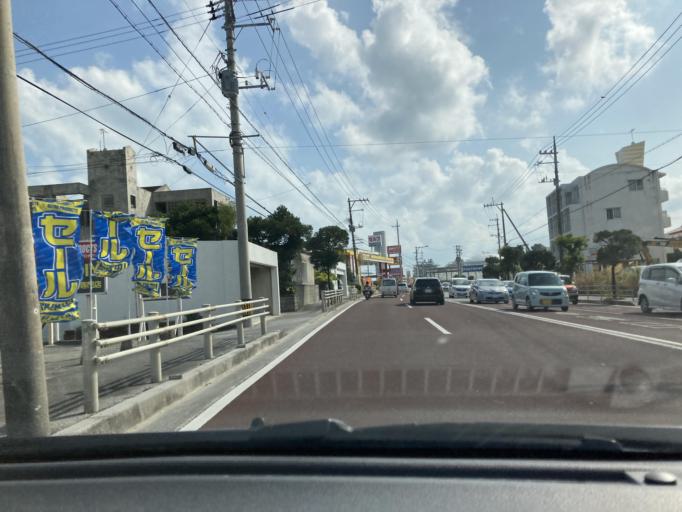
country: JP
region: Okinawa
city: Chatan
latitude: 26.2832
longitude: 127.8155
